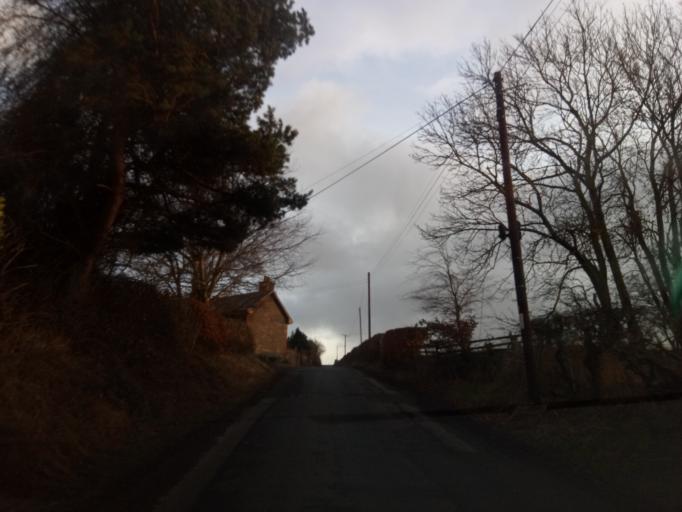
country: GB
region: Scotland
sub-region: The Scottish Borders
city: Selkirk
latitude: 55.5711
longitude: -2.8132
